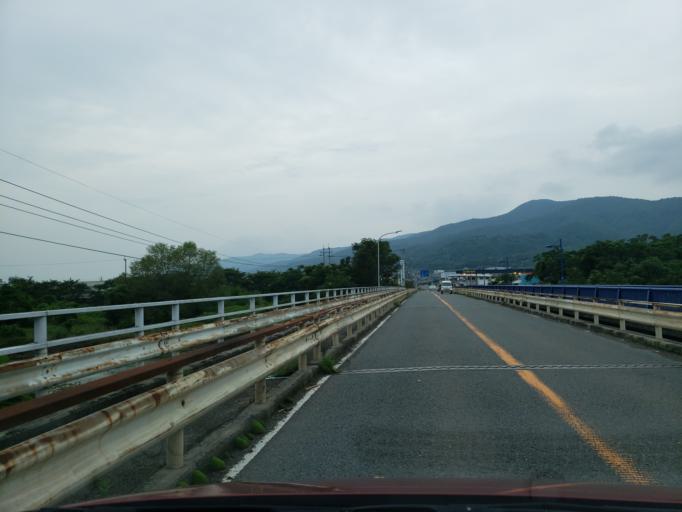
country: JP
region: Tokushima
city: Kamojimacho-jogejima
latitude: 34.1024
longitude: 134.2769
